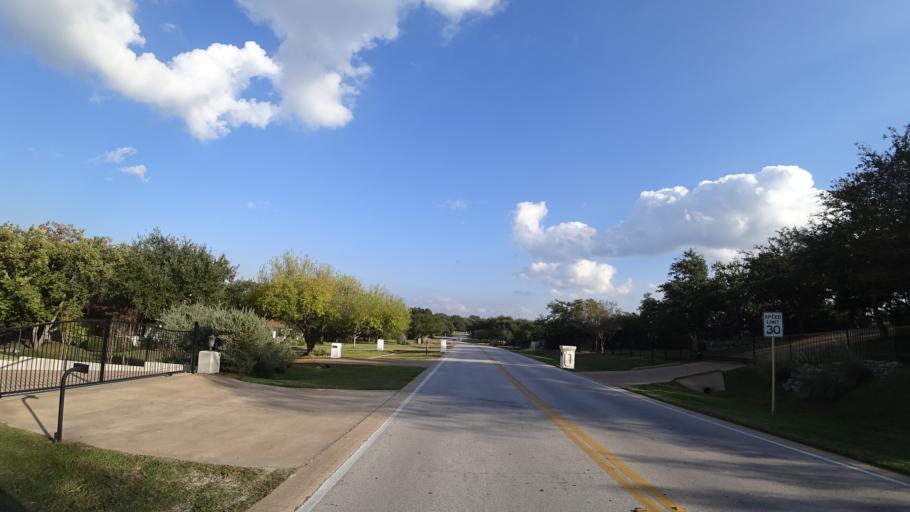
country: US
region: Texas
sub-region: Travis County
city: Barton Creek
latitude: 30.2839
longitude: -97.8748
